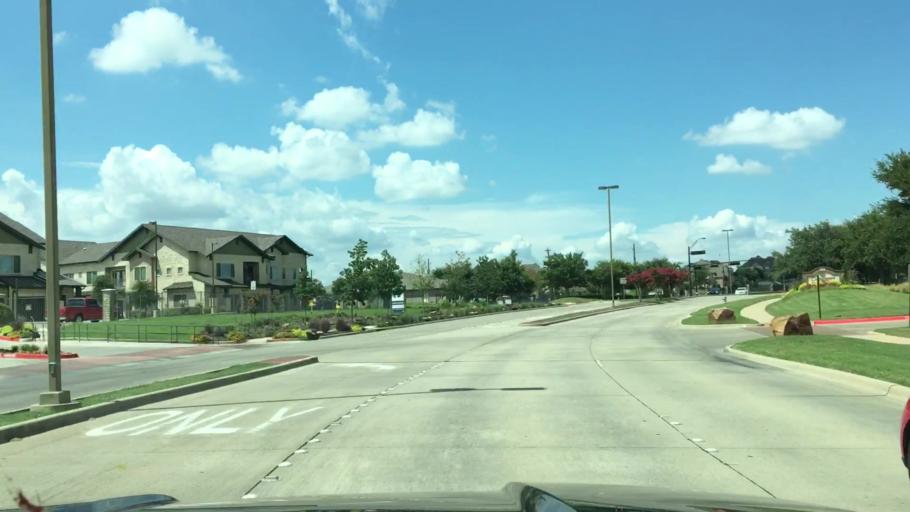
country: US
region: Texas
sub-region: Tarrant County
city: Keller
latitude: 32.9400
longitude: -97.2427
